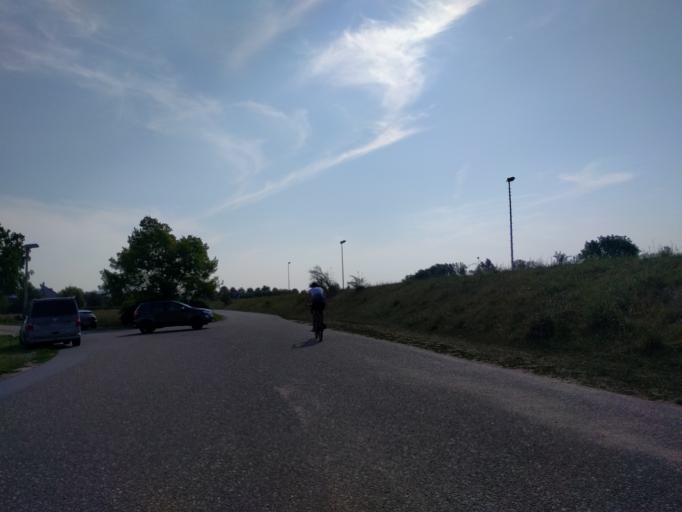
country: DE
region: Bavaria
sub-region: Upper Palatinate
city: Tegernheim
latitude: 49.0183
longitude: 12.1702
